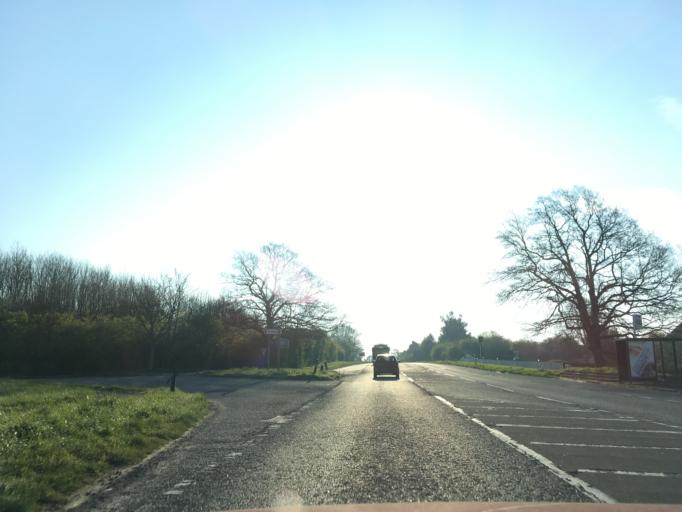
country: GB
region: England
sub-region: Oxfordshire
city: Eynsham
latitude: 51.7871
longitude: -1.3873
